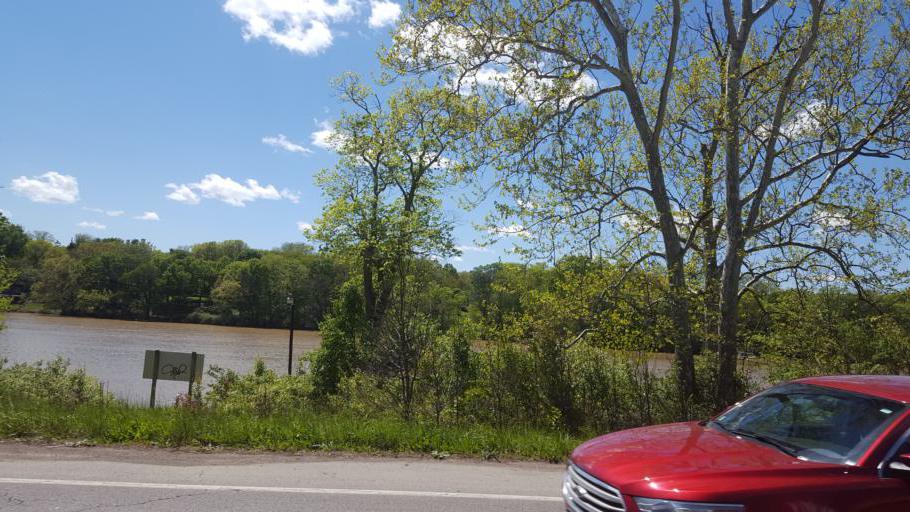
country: US
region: Ohio
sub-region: Franklin County
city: Dublin
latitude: 40.0711
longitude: -83.1065
